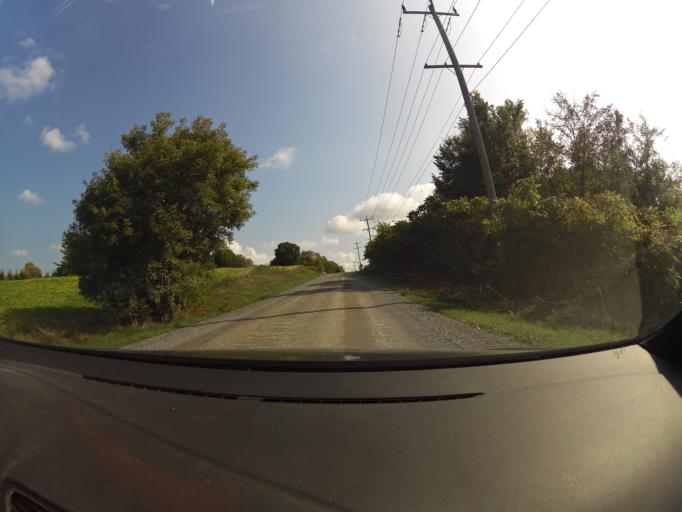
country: CA
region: Ontario
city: Arnprior
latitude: 45.4177
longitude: -76.2462
